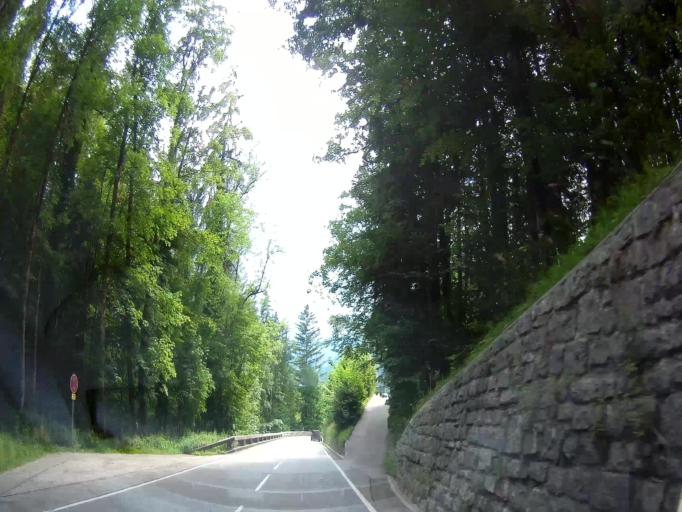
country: DE
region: Bavaria
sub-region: Upper Bavaria
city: Marktschellenberg
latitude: 47.6532
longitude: 13.0501
